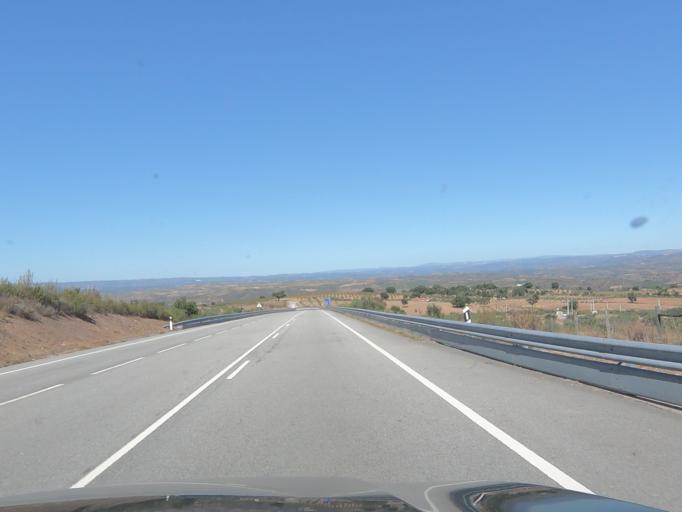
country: PT
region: Braganca
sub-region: Mirandela
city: Mirandela
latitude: 41.4832
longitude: -7.2243
